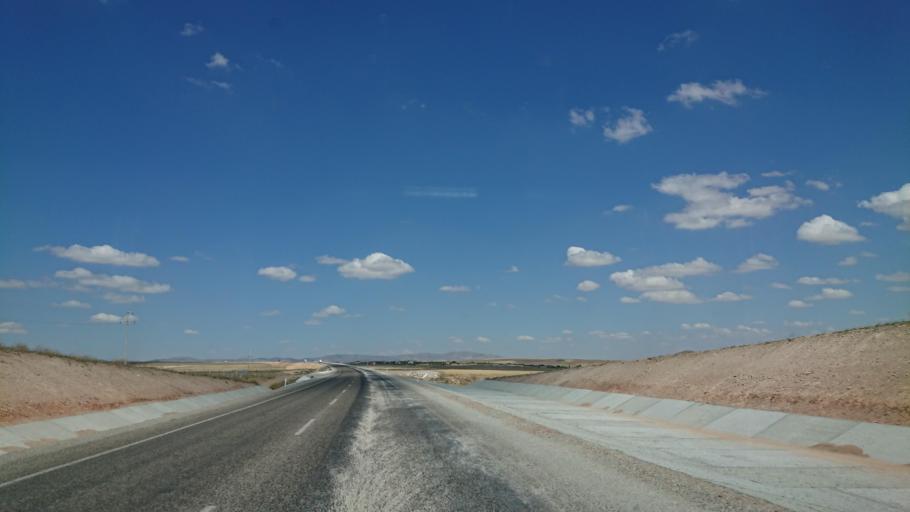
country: TR
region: Kirsehir
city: Kirsehir
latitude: 39.1221
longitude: 34.0163
